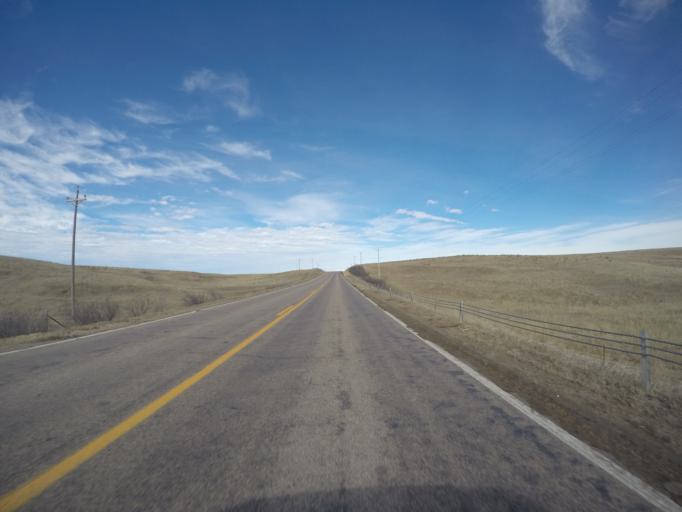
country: US
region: Nebraska
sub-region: Franklin County
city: Franklin
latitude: 40.1407
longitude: -98.9524
